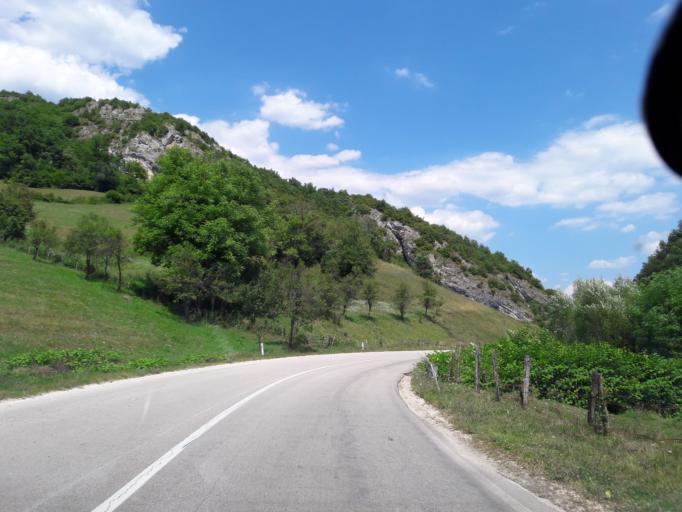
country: BA
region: Republika Srpska
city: Mrkonjic Grad
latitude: 44.4231
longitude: 17.1214
